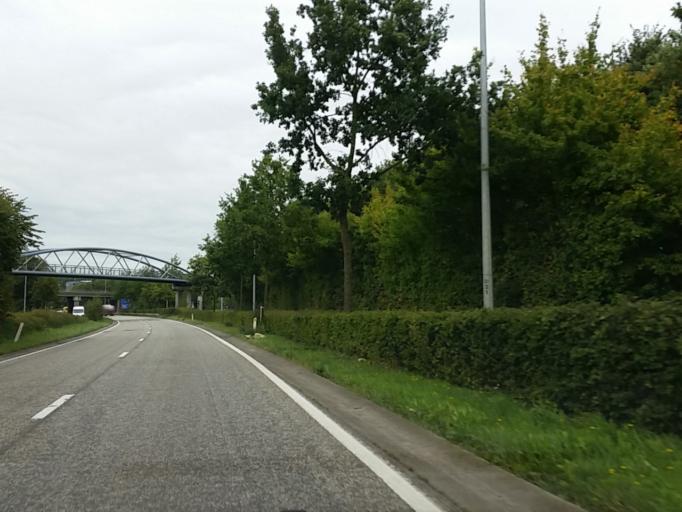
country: BE
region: Flanders
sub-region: Provincie Vlaams-Brabant
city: Vilvoorde
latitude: 50.9418
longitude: 4.4483
